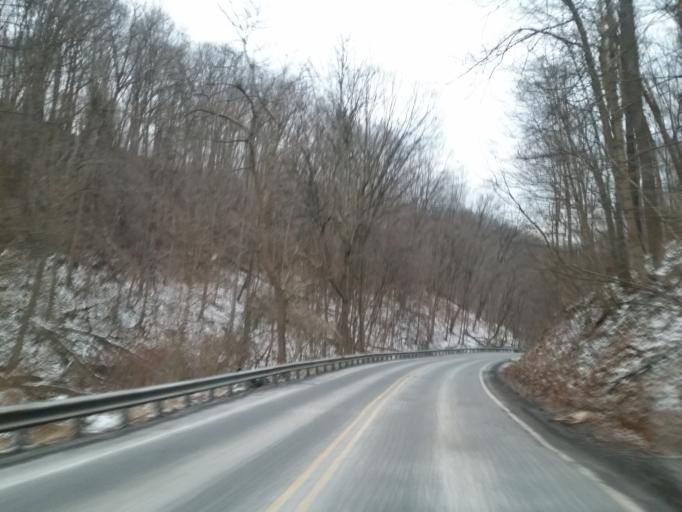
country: US
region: Pennsylvania
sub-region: Allegheny County
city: Brentwood
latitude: 40.3900
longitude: -79.9469
